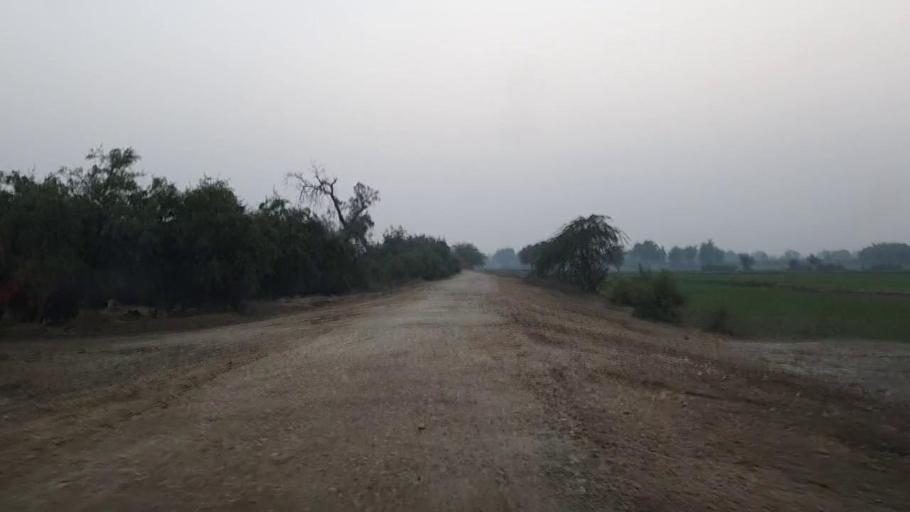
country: PK
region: Sindh
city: Karaundi
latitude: 26.9532
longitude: 68.4536
